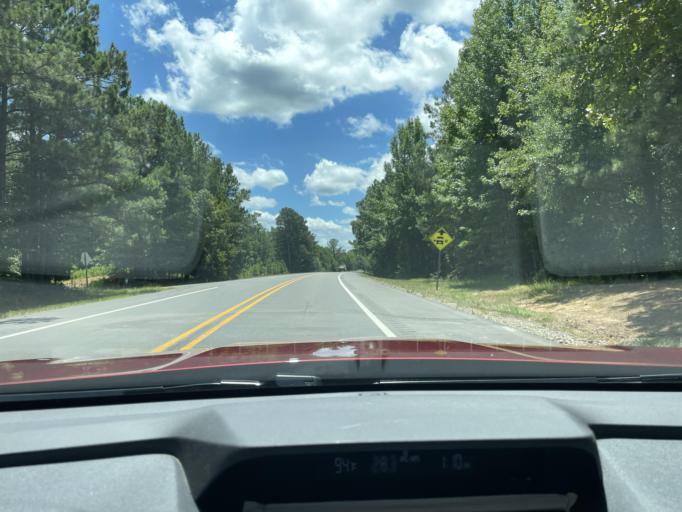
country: US
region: Arkansas
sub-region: Drew County
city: Monticello
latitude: 33.7223
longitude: -91.8104
